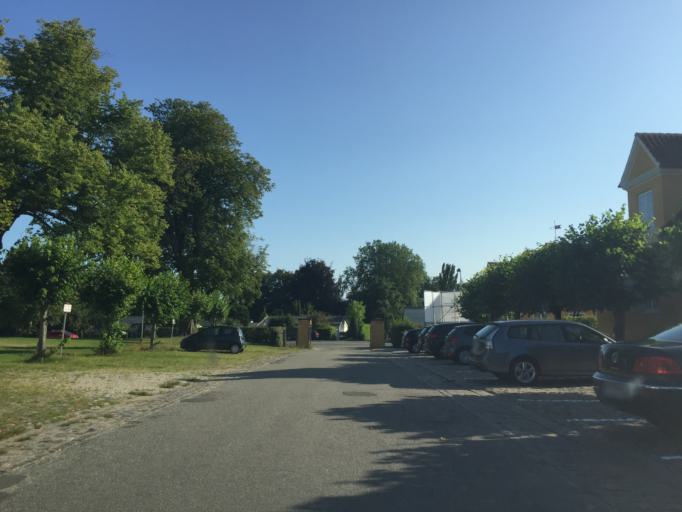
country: DK
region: Capital Region
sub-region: Lyngby-Tarbaek Kommune
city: Kongens Lyngby
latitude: 55.7624
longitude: 12.5393
